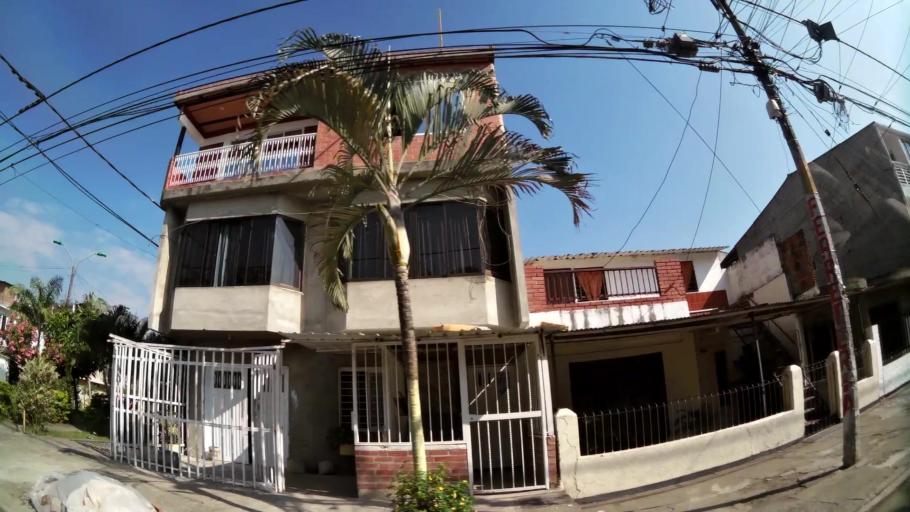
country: CO
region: Valle del Cauca
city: Cali
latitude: 3.4162
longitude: -76.5252
